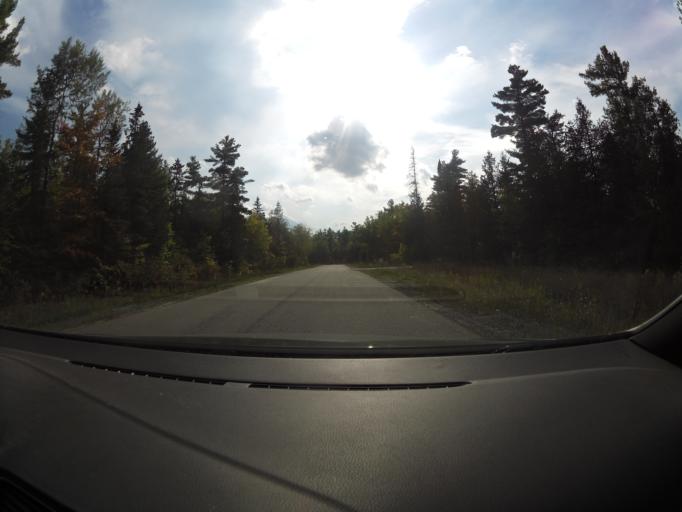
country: CA
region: Ontario
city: Carleton Place
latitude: 45.3388
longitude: -76.1619
